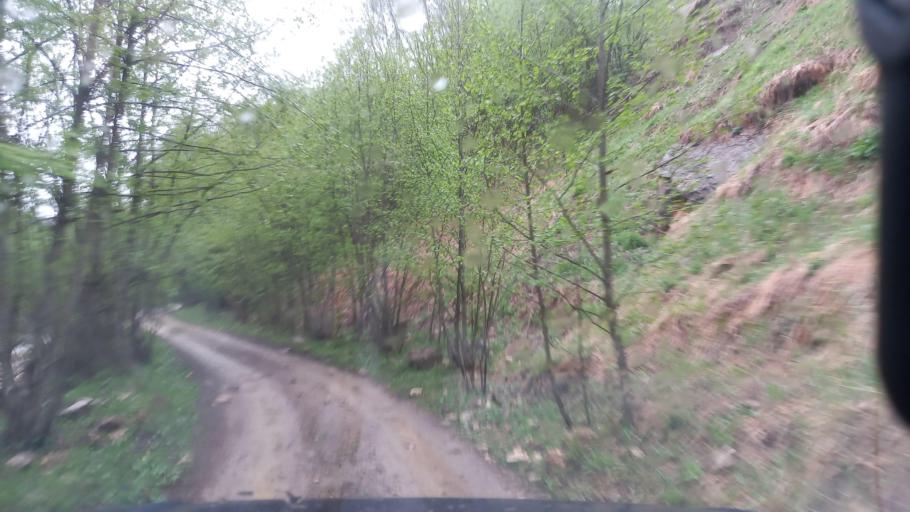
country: RU
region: Kabardino-Balkariya
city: Bylym
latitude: 43.6001
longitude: 42.9324
